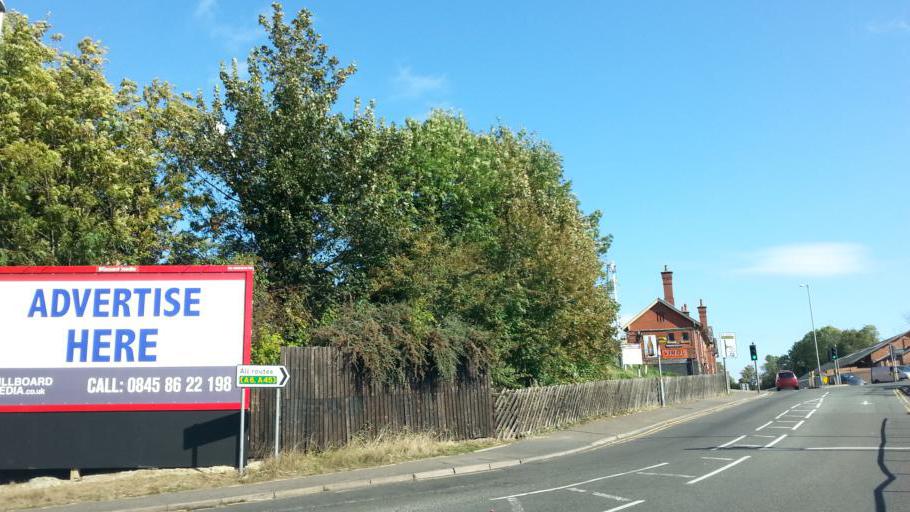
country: GB
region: England
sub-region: Northamptonshire
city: Rushden
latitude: 52.2940
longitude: -0.5992
